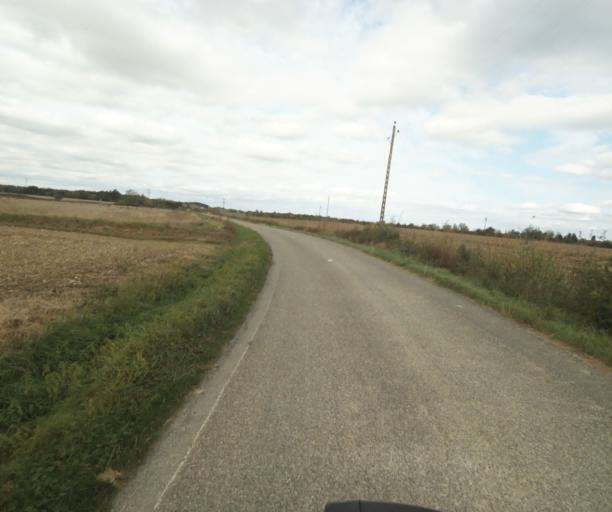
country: FR
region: Midi-Pyrenees
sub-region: Departement du Tarn-et-Garonne
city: Finhan
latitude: 43.8700
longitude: 1.1495
